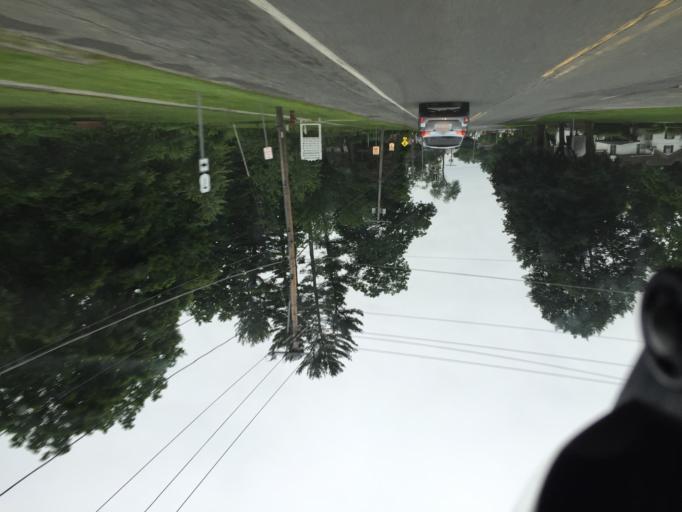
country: US
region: Massachusetts
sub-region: Berkshire County
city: Sheffield
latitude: 42.1125
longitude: -73.3515
